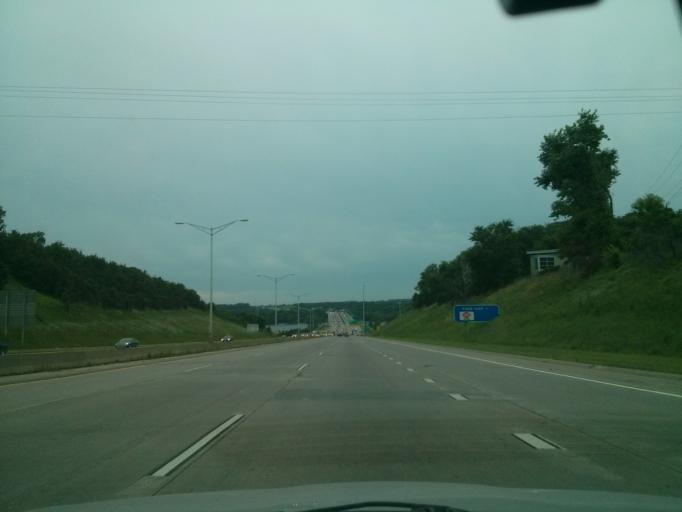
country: US
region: Wisconsin
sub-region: Saint Croix County
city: Hudson
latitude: 44.9629
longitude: -92.7459
